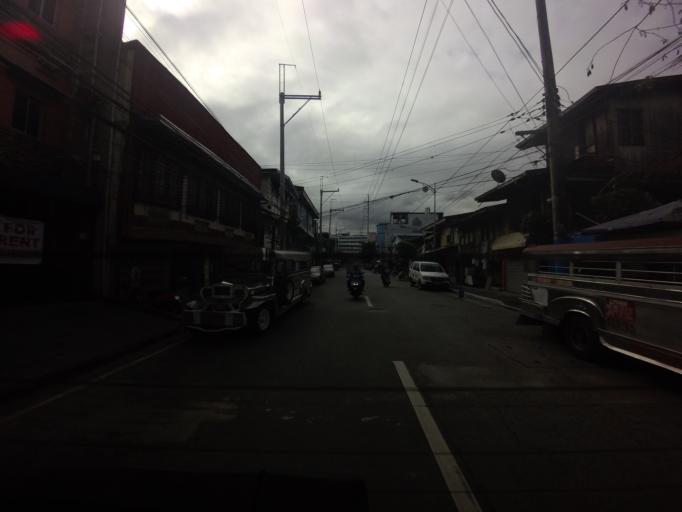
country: PH
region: Metro Manila
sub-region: City of Manila
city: Quiapo
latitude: 14.6034
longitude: 121.0010
